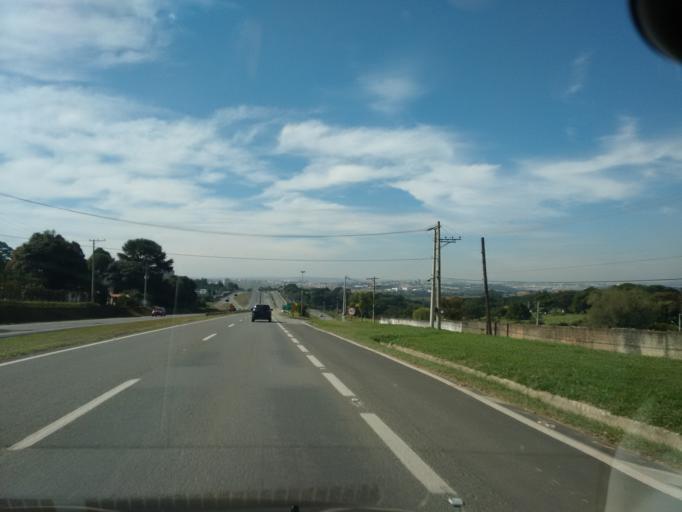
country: BR
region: Sao Paulo
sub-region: Itu
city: Itu
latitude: -23.2546
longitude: -47.3543
